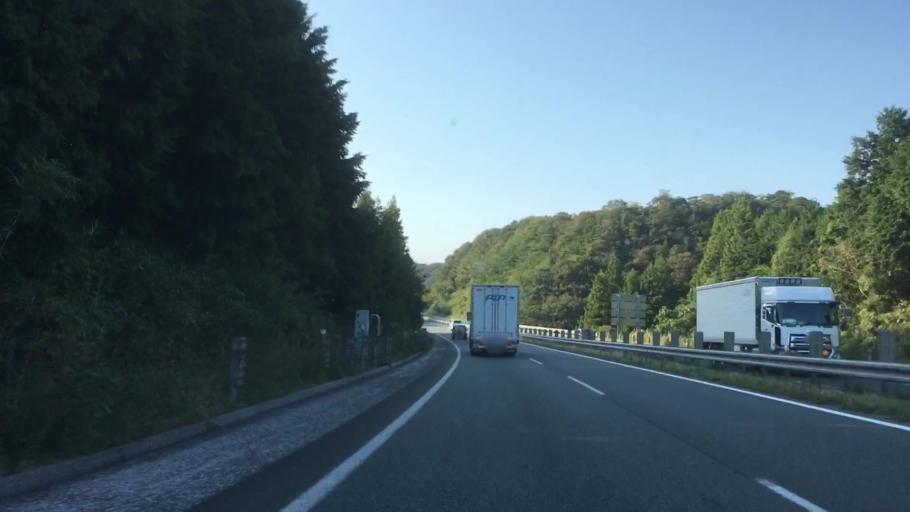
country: JP
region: Yamaguchi
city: Ogori-shimogo
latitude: 34.1597
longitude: 131.3307
